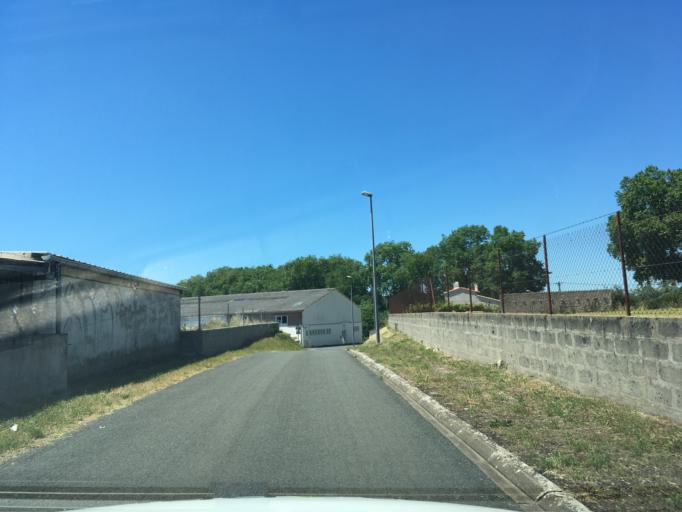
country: FR
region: Poitou-Charentes
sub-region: Departement des Deux-Sevres
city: Niort
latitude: 46.3328
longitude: -0.4301
